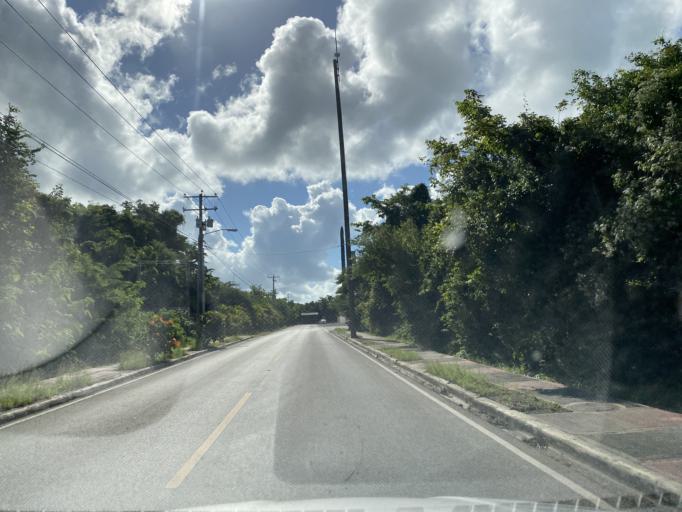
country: DO
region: La Altagracia
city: San Rafael del Yuma
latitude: 18.3347
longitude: -68.8089
